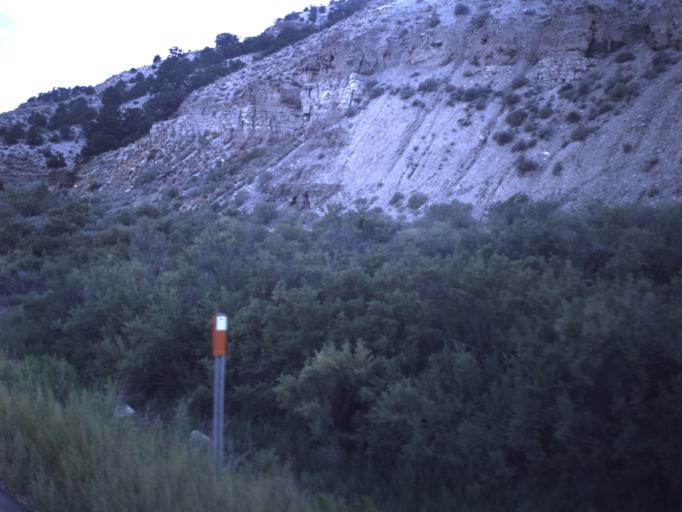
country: US
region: Utah
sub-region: Duchesne County
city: Duchesne
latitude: 40.1056
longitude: -110.4688
